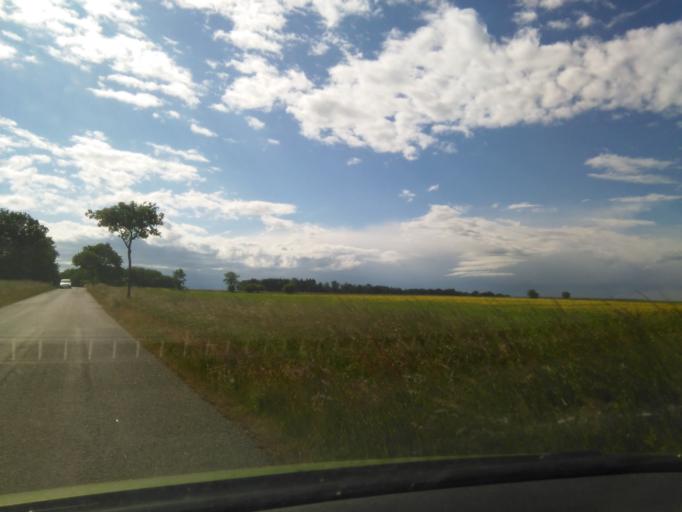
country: DK
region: Capital Region
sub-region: Bornholm Kommune
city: Nexo
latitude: 55.1243
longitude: 15.0782
